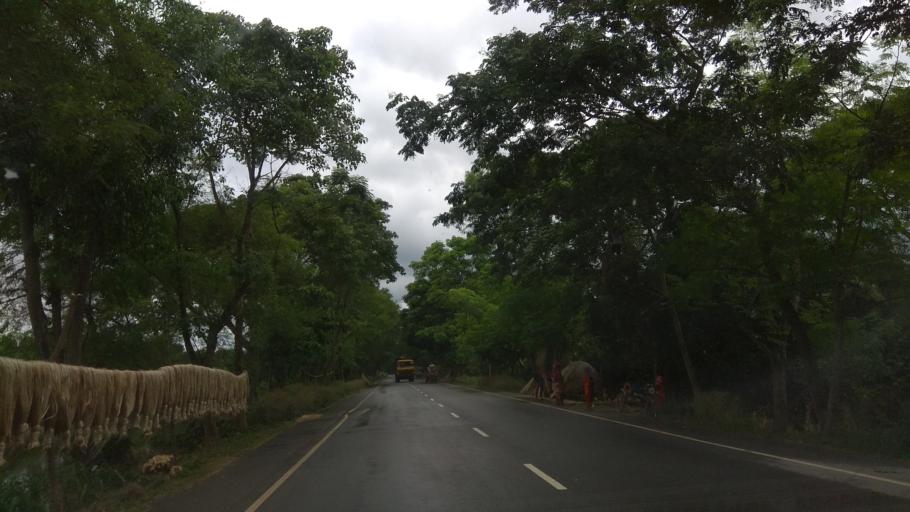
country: BD
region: Khulna
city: Kalia
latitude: 23.2390
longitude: 89.7488
